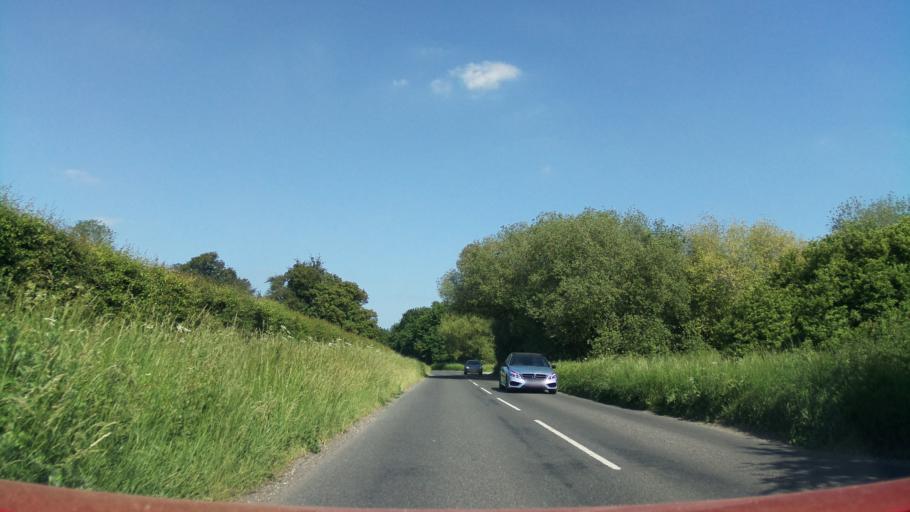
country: GB
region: England
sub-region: Hampshire
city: Andover
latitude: 51.2212
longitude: -1.5164
